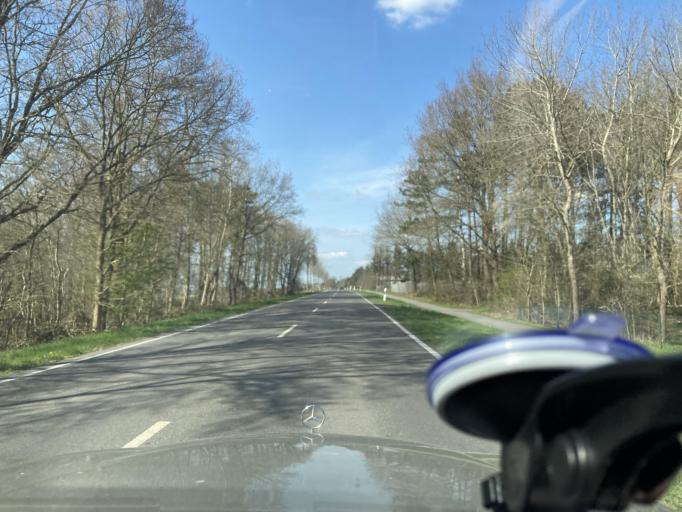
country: DE
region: Schleswig-Holstein
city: Stelle-Wittenwurth
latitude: 54.2757
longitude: 9.0469
